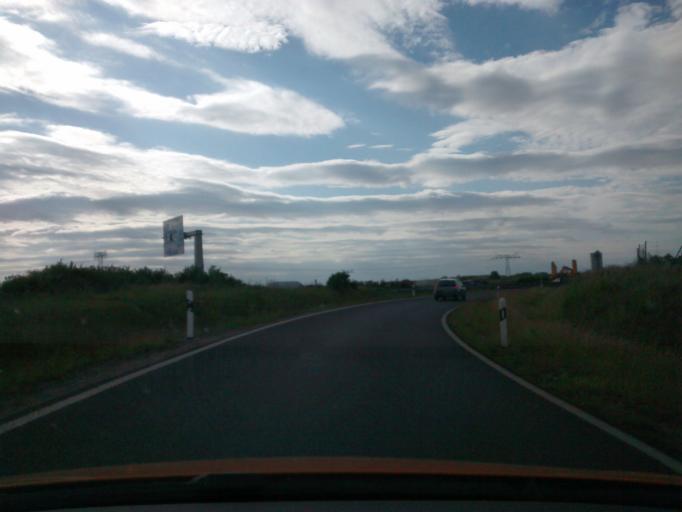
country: DE
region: Brandenburg
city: Schulzendorf
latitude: 52.3652
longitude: 13.5497
